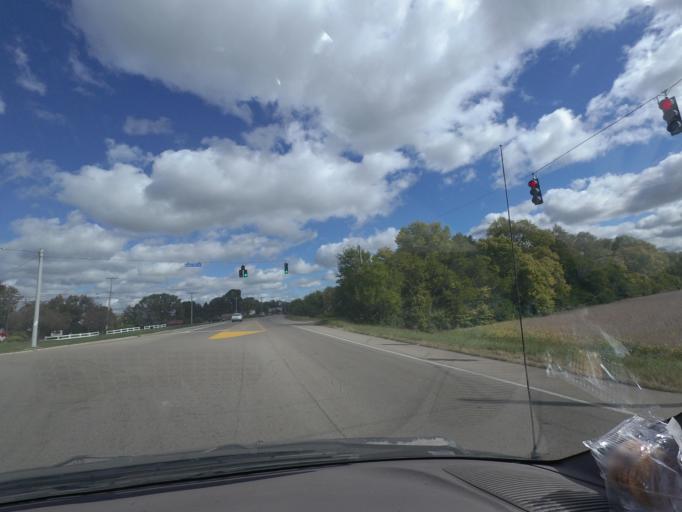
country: US
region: Ohio
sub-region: Clark County
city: Park Layne
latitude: 39.8723
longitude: -84.0552
